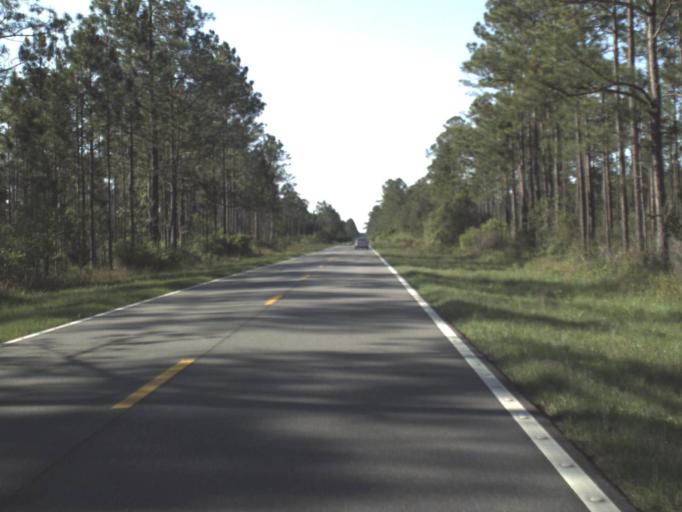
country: US
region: Florida
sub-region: Gulf County
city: Wewahitchka
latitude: 30.1016
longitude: -84.9858
